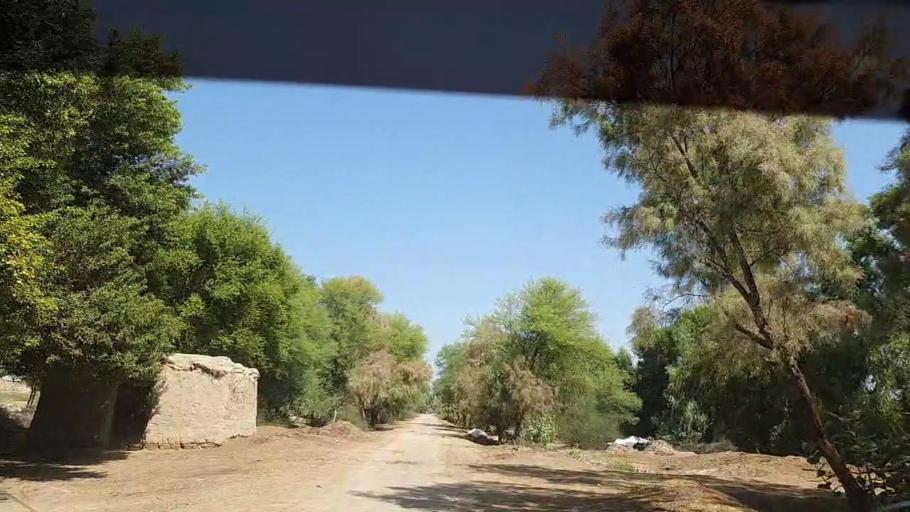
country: PK
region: Sindh
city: Tangwani
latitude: 28.2906
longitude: 69.0733
